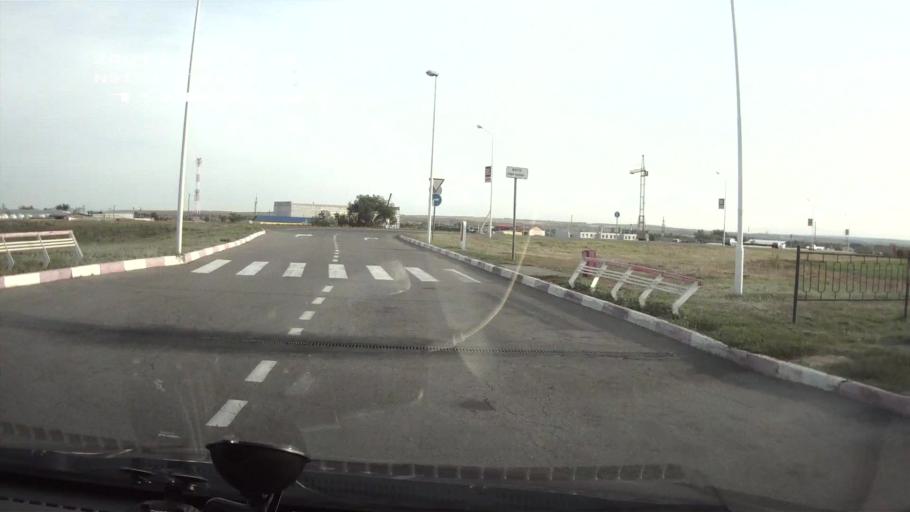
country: RU
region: Saratov
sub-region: Saratovskiy Rayon
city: Saratov
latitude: 51.7355
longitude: 46.0359
